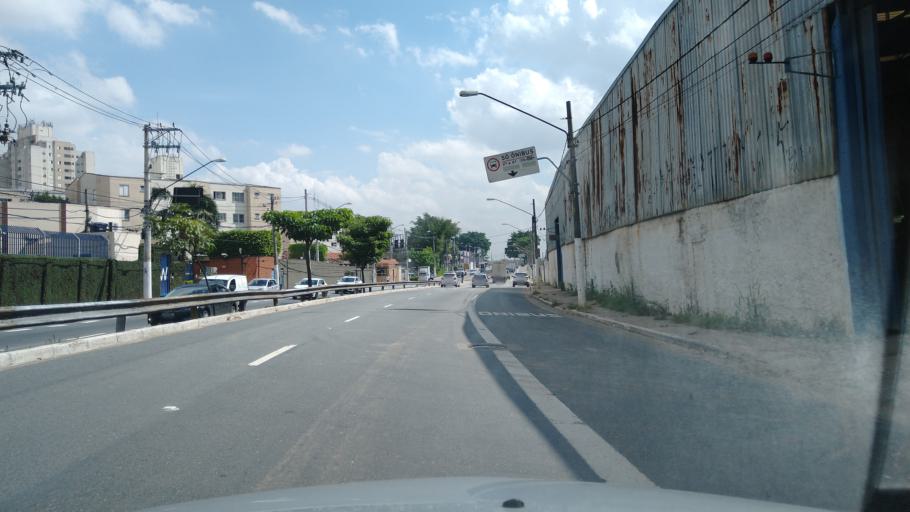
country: BR
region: Sao Paulo
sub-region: Guarulhos
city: Guarulhos
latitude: -23.4960
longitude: -46.5102
